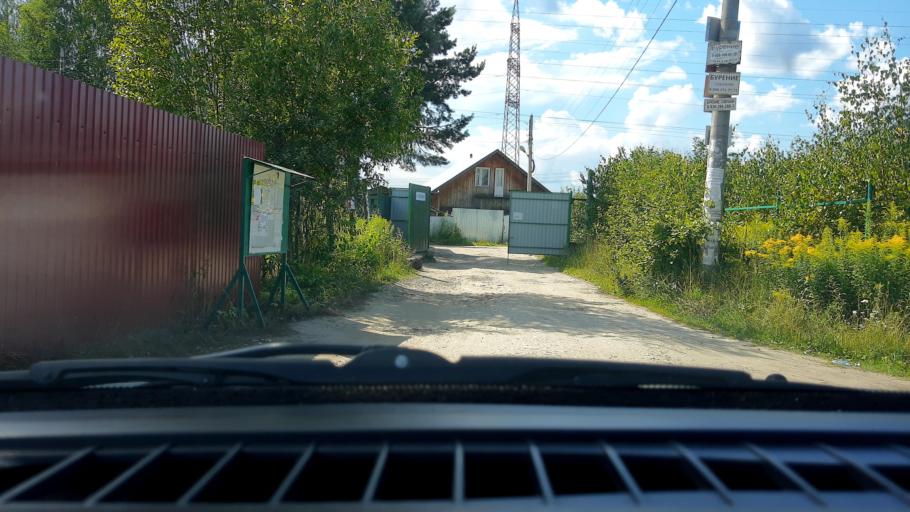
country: RU
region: Nizjnij Novgorod
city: Gorbatovka
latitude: 56.3342
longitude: 43.6676
